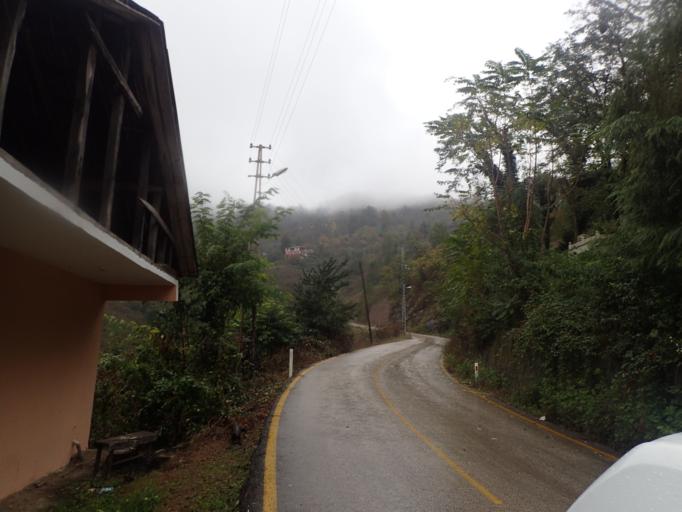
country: TR
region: Ordu
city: Persembe
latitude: 41.0387
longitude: 37.7285
